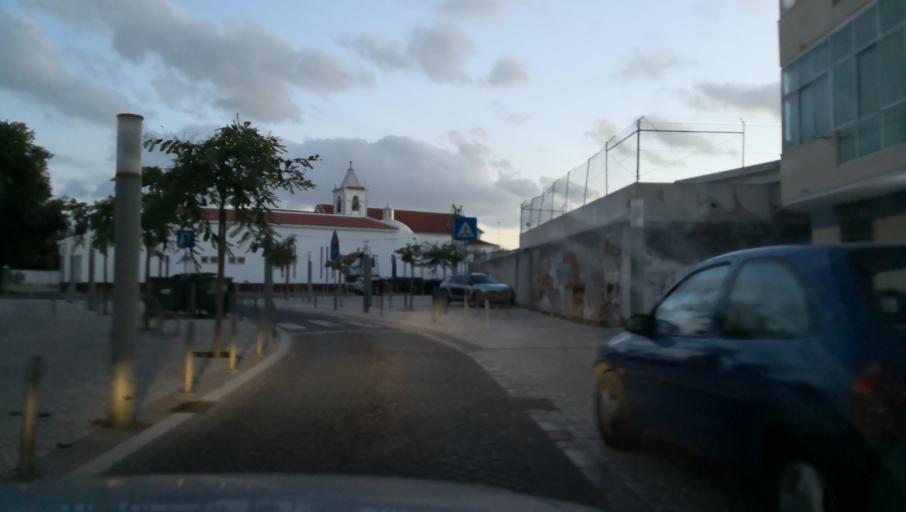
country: PT
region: Setubal
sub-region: Moita
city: Alhos Vedros
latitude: 38.6545
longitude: -9.0289
